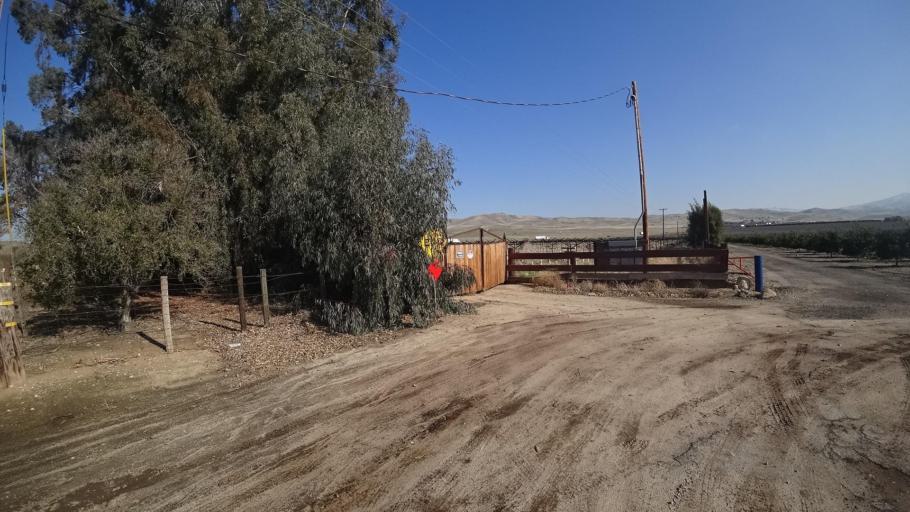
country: US
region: California
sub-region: Kern County
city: Arvin
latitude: 35.2968
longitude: -118.7710
